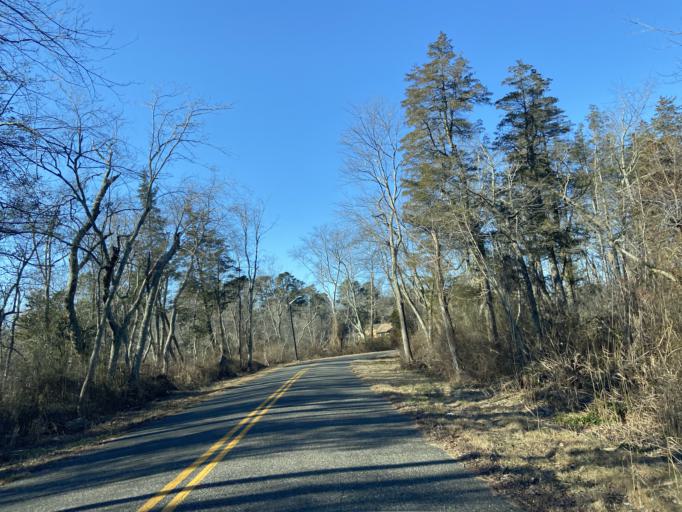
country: US
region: New Jersey
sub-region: Cumberland County
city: Vineland
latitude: 39.4924
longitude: -75.0727
